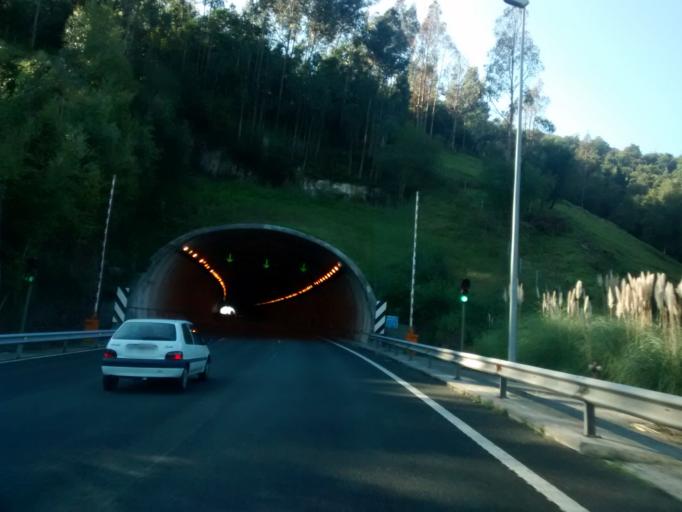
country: ES
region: Cantabria
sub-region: Provincia de Cantabria
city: Cartes
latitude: 43.3070
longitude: -4.0791
